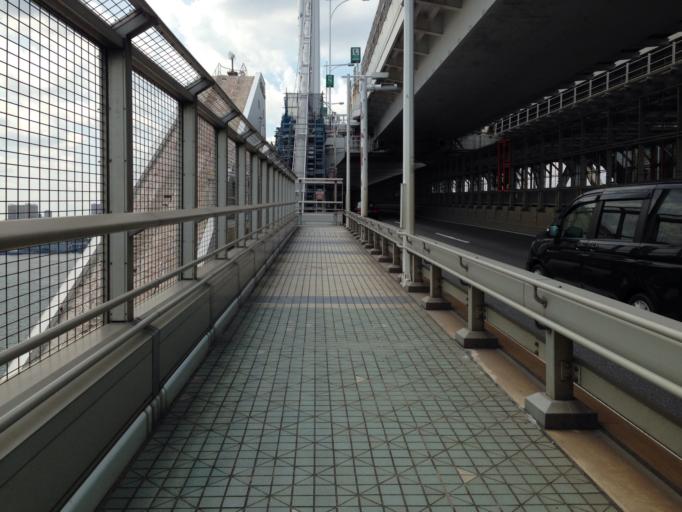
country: JP
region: Tokyo
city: Tokyo
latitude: 35.6351
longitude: 139.7679
